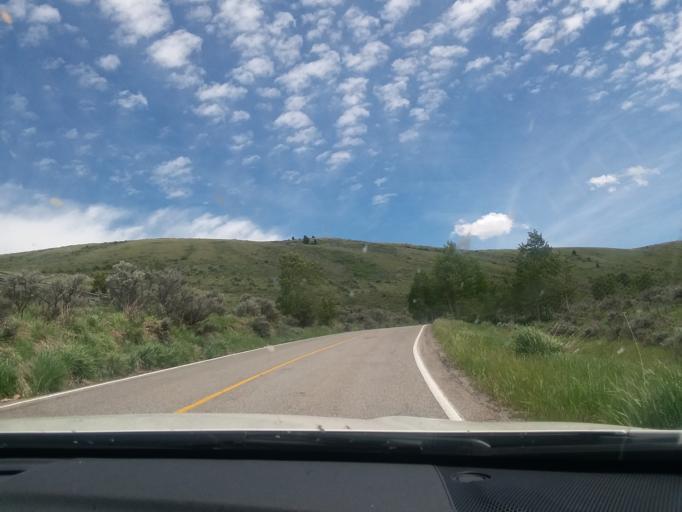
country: US
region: Wyoming
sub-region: Teton County
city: Jackson
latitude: 43.4966
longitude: -110.7772
